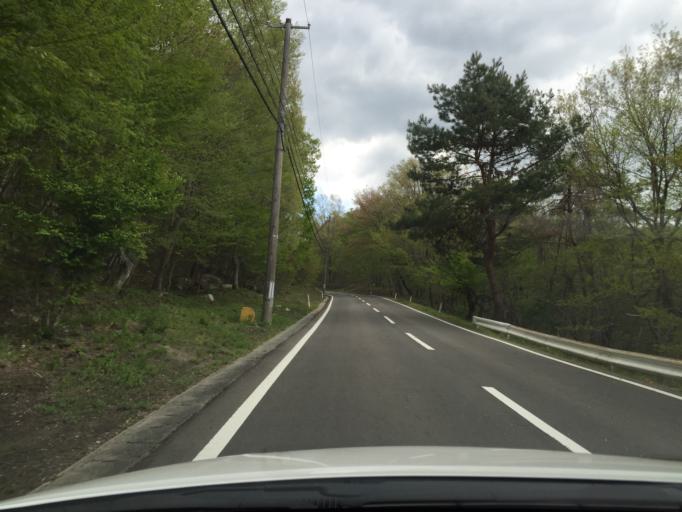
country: JP
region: Miyagi
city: Marumori
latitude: 37.6874
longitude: 140.7920
